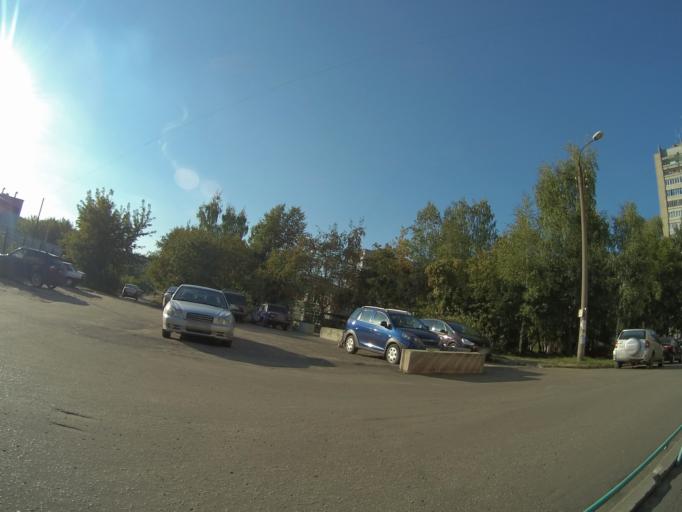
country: RU
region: Vladimir
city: Vladimir
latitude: 56.1489
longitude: 40.3721
